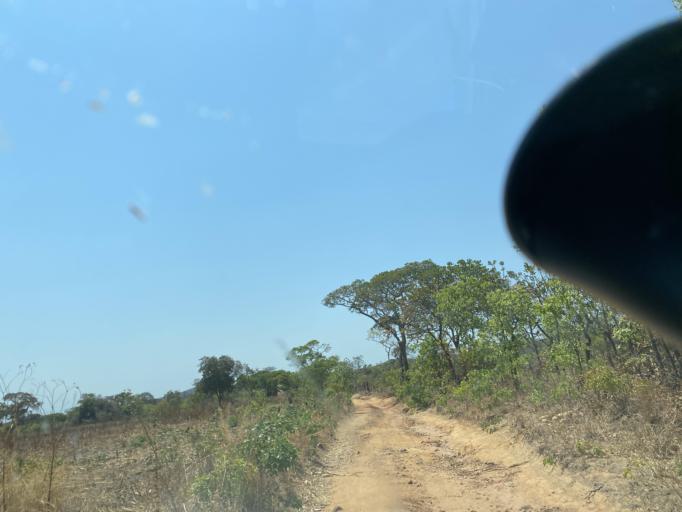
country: ZM
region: Lusaka
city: Chongwe
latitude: -15.4269
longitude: 29.1828
